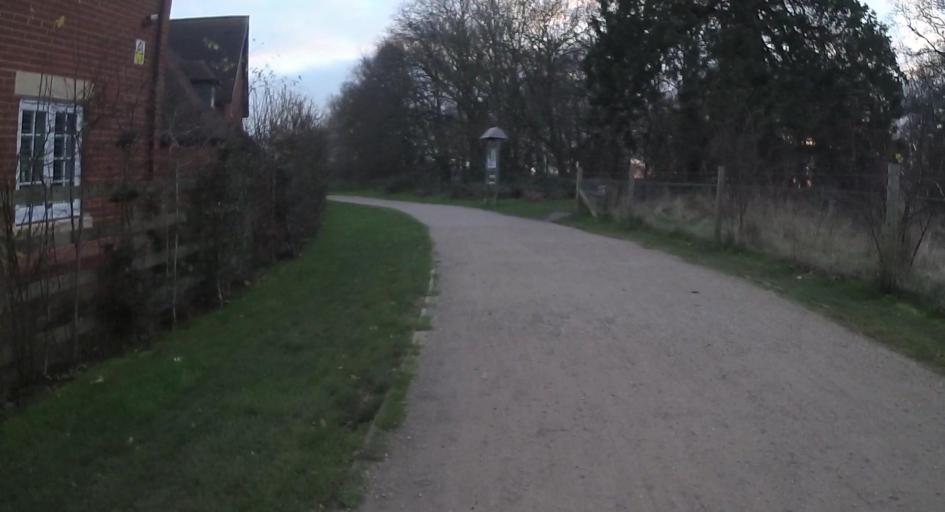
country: GB
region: England
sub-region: Bracknell Forest
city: Bracknell
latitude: 51.4301
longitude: -0.7623
